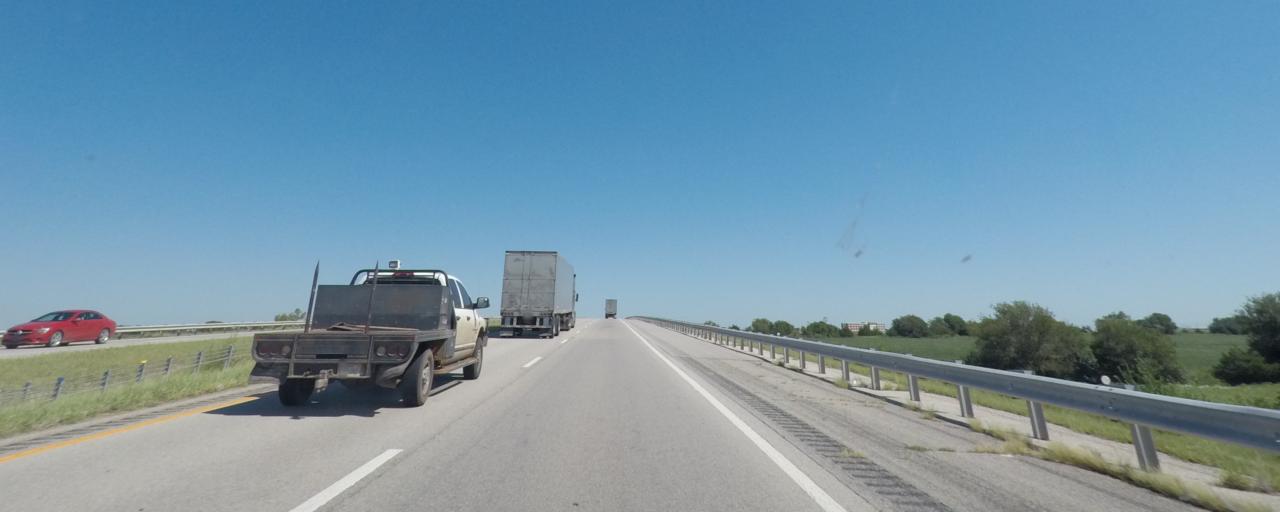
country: US
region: Oklahoma
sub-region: Kay County
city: Blackwell
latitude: 36.8011
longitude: -97.3438
